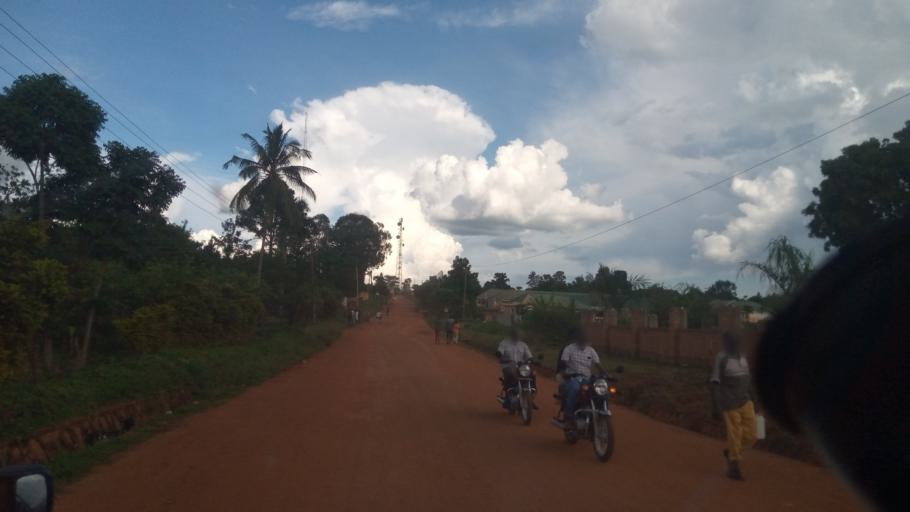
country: UG
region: Northern Region
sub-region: Lira District
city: Lira
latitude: 2.2381
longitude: 32.9004
